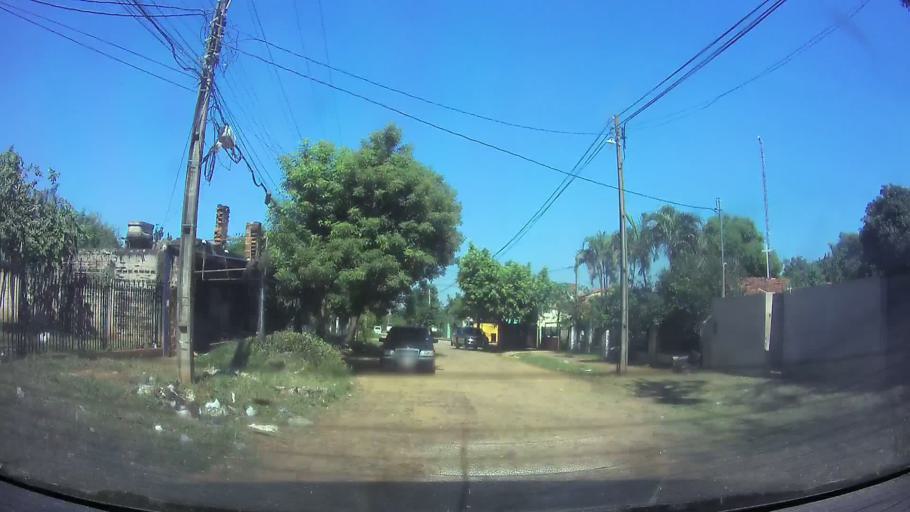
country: PY
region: Central
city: Fernando de la Mora
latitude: -25.3019
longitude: -57.5273
